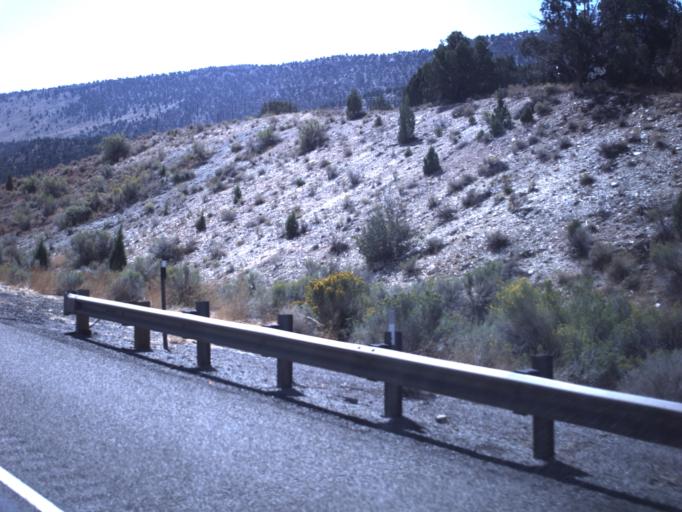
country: US
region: Utah
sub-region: Sevier County
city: Salina
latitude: 38.9286
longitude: -111.7845
